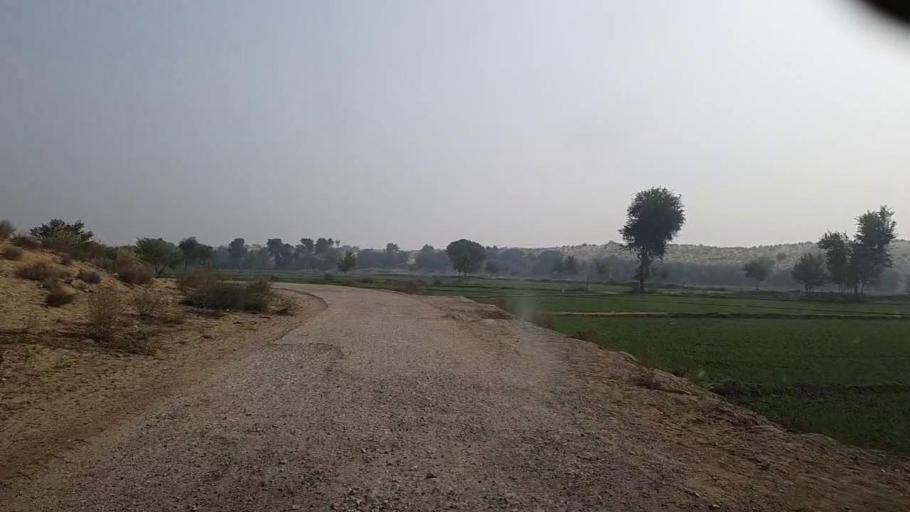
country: PK
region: Sindh
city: Bozdar
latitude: 27.0572
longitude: 68.6573
